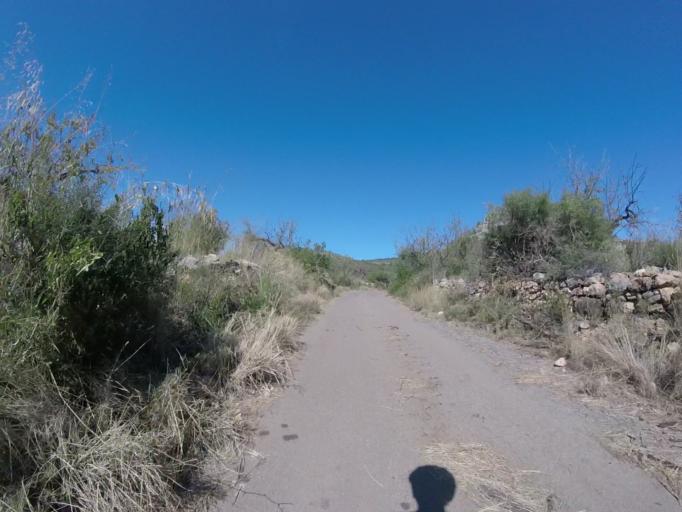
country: ES
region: Valencia
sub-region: Provincia de Castello
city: Orpesa/Oropesa del Mar
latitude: 40.1355
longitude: 0.1051
